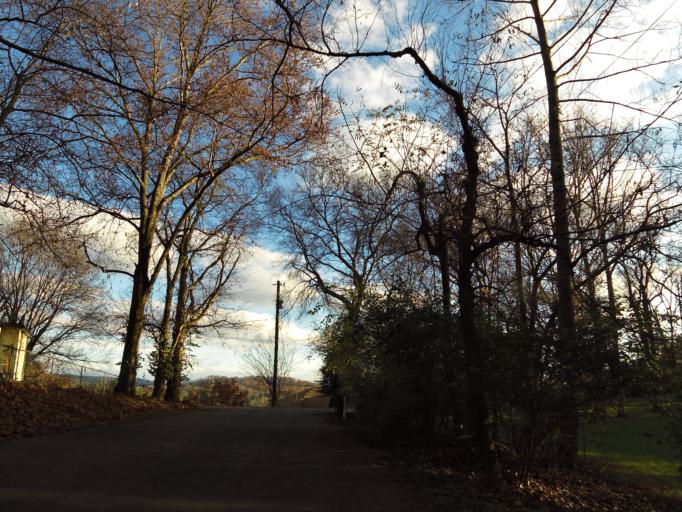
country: US
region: Tennessee
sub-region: Blount County
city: Alcoa
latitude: 35.8705
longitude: -83.9711
